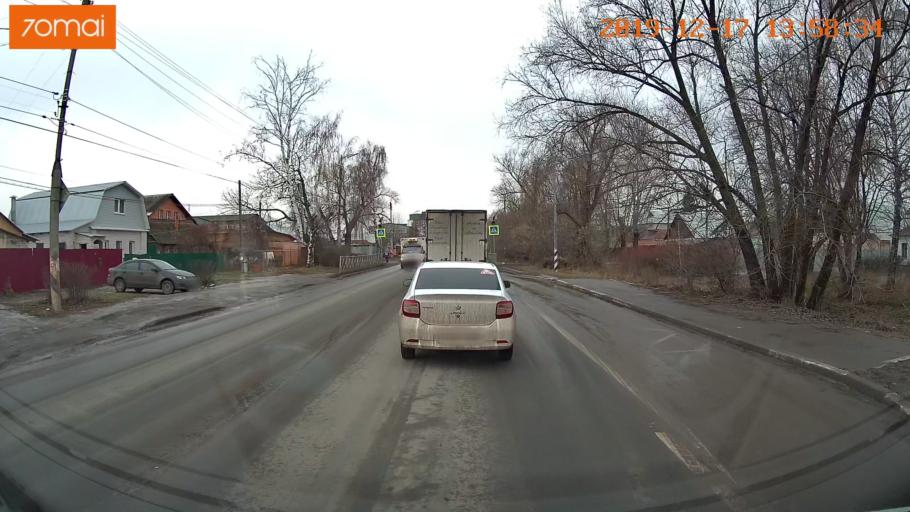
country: RU
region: Rjazan
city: Ryazan'
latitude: 54.6228
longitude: 39.6832
